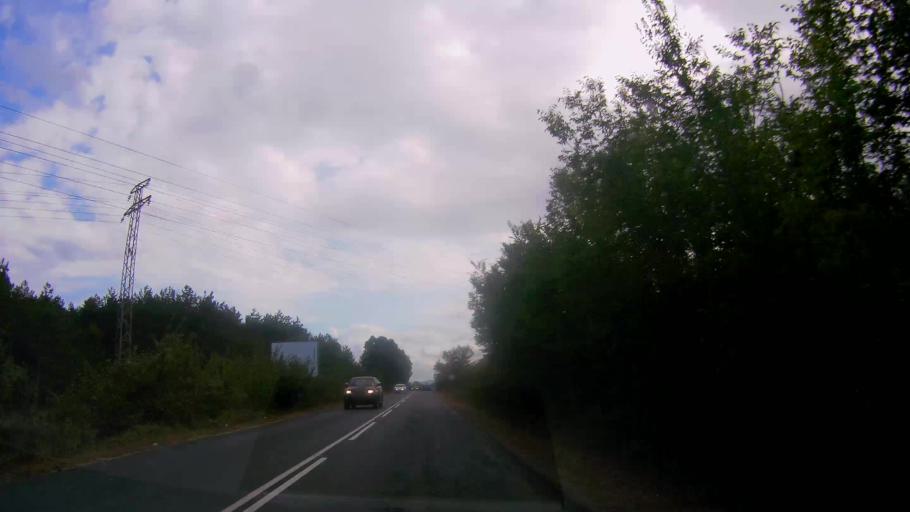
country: BG
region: Burgas
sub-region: Obshtina Primorsko
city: Primorsko
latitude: 42.2733
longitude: 27.7413
